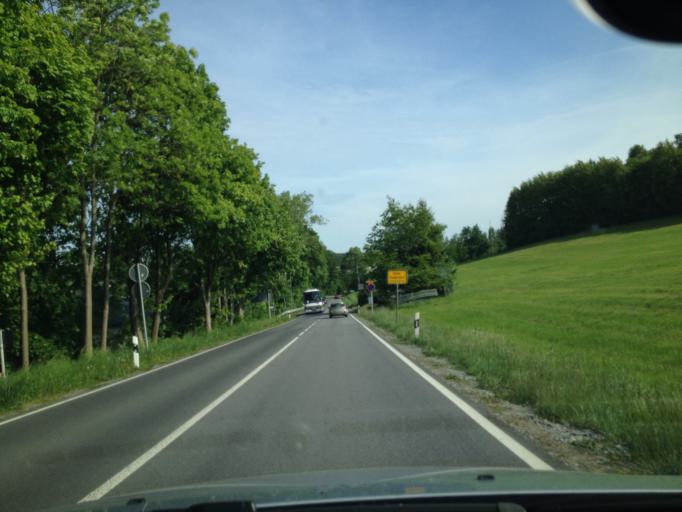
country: DE
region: Saxony
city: Ehrenfriedersdorf
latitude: 50.6372
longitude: 12.9659
